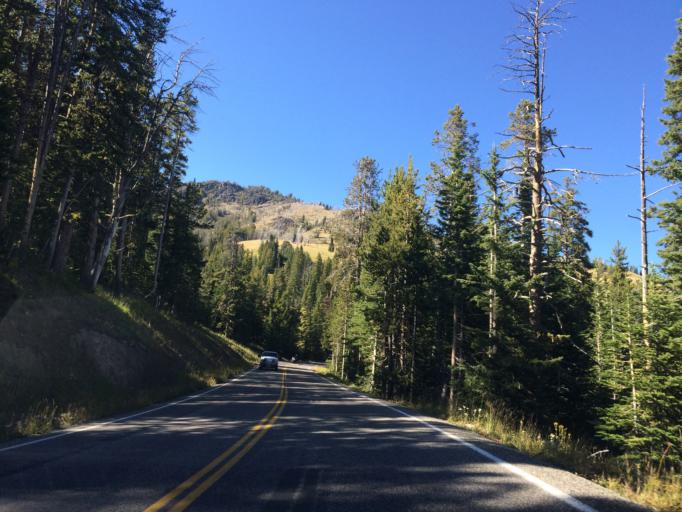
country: US
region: Montana
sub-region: Gallatin County
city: West Yellowstone
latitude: 44.7750
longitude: -110.4591
